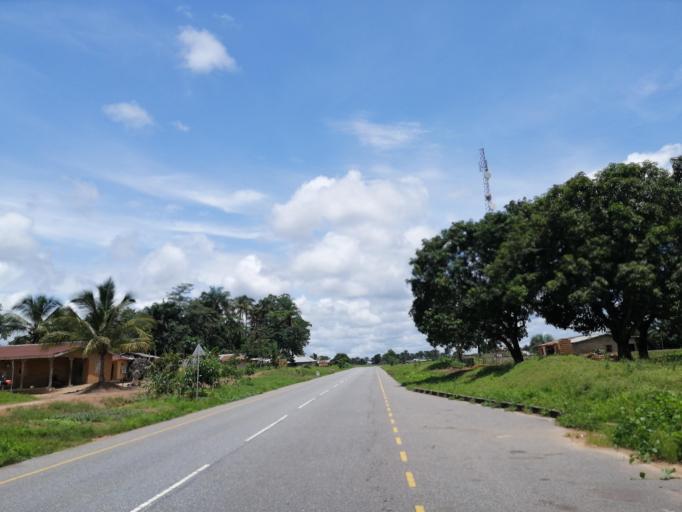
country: SL
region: Northern Province
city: Pepel
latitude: 8.6882
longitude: -12.9989
